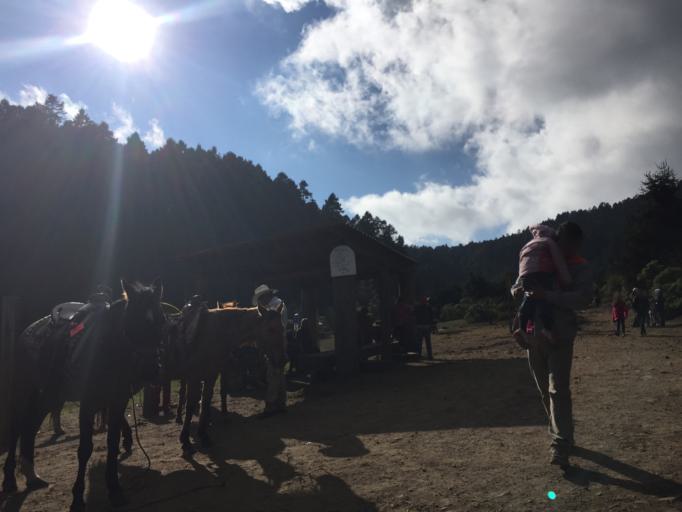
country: MX
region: Michoacan
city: Mineral de Angangueo
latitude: 19.6695
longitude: -100.2805
